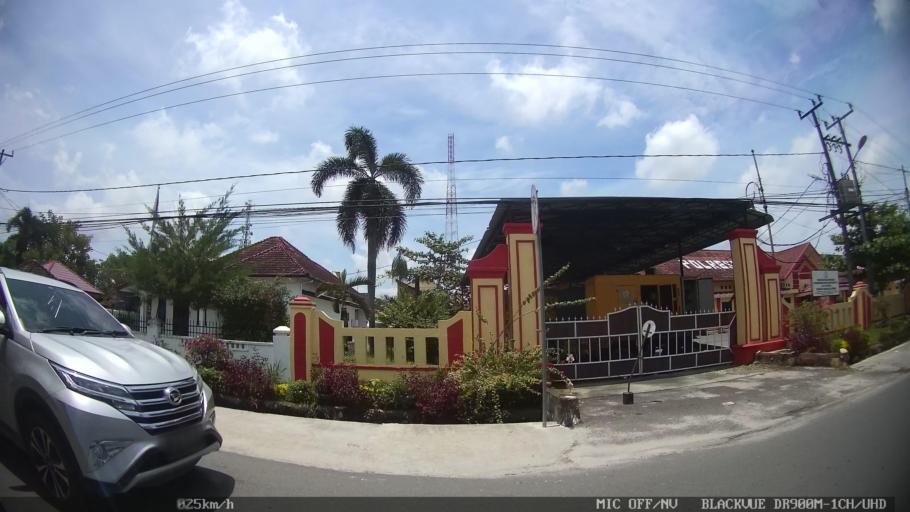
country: ID
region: North Sumatra
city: Percut
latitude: 3.5589
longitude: 98.8611
